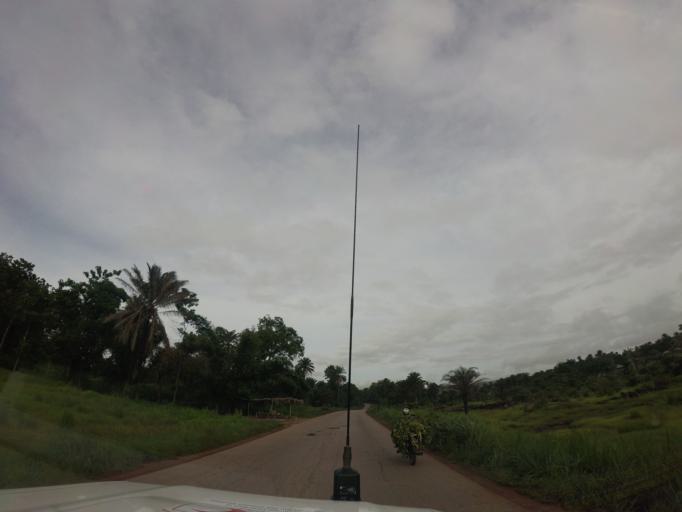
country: GN
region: Kindia
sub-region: Kindia
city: Kindia
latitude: 9.9432
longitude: -12.9677
